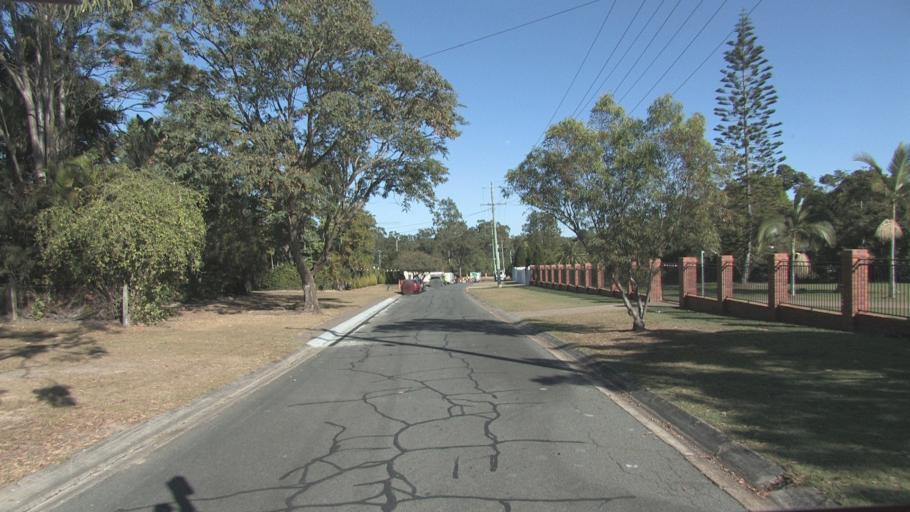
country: AU
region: Queensland
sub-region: Logan
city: Park Ridge South
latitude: -27.6735
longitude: 153.0156
